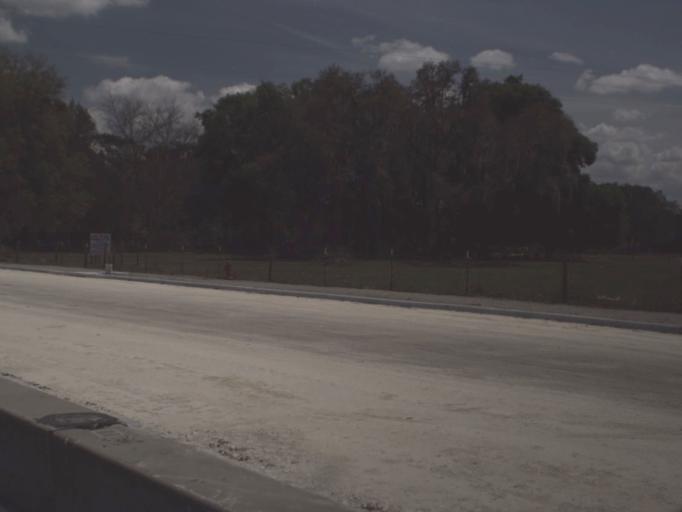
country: US
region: Florida
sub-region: Sumter County
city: Bushnell
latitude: 28.6686
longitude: -82.1306
